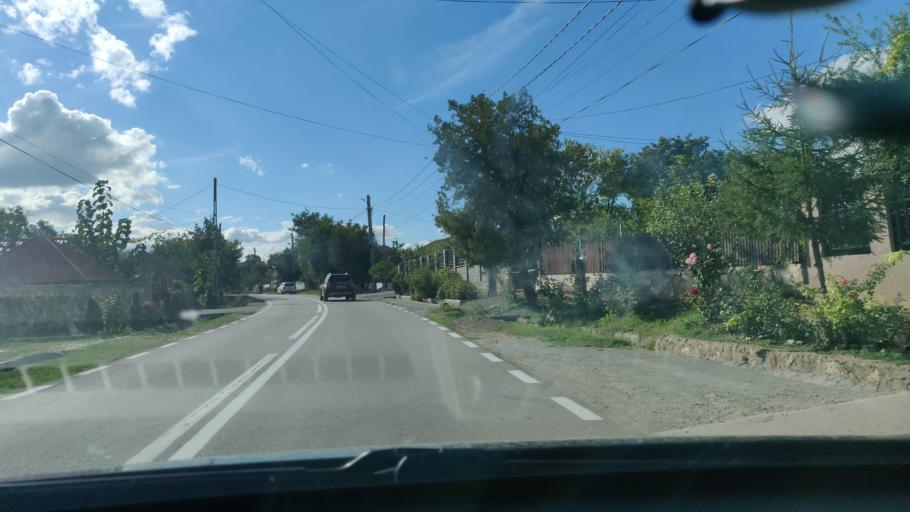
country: RO
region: Constanta
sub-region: Comuna Albesti
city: Albesti
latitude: 43.8242
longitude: 28.3474
